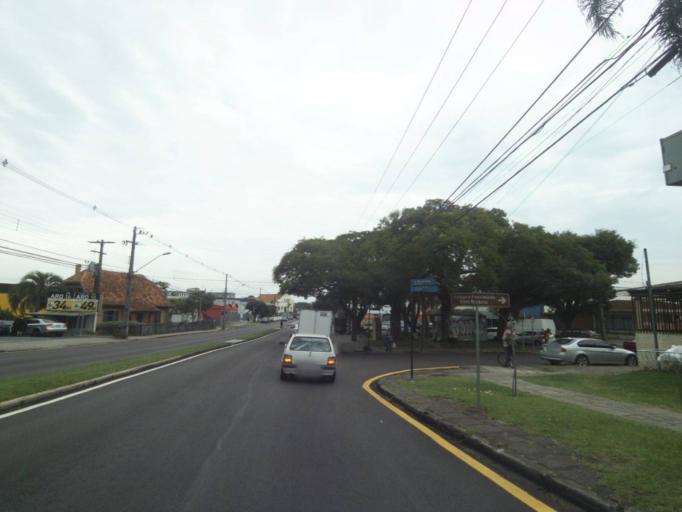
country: BR
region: Parana
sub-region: Curitiba
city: Curitiba
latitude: -25.4187
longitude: -49.2935
